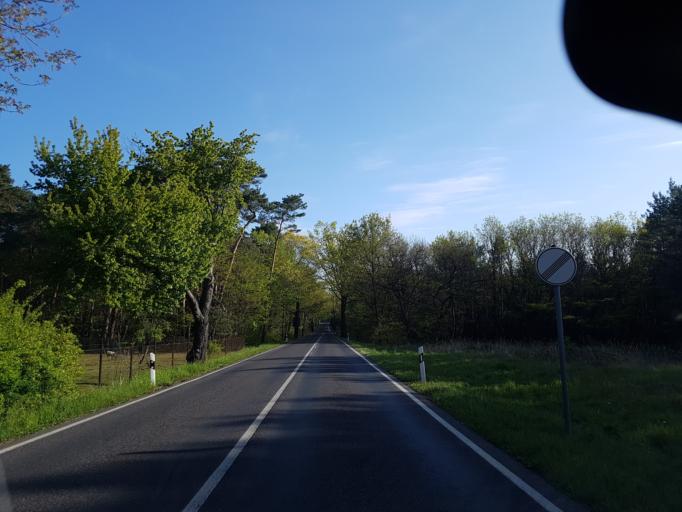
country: DE
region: Brandenburg
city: Grossraschen
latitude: 51.6119
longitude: 14.0212
